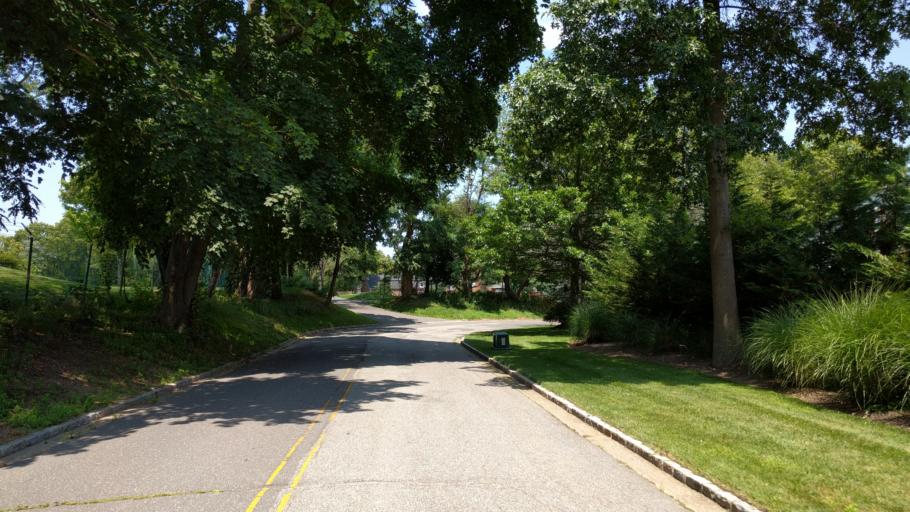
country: US
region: New York
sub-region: Nassau County
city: Syosset
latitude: 40.8205
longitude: -73.5115
